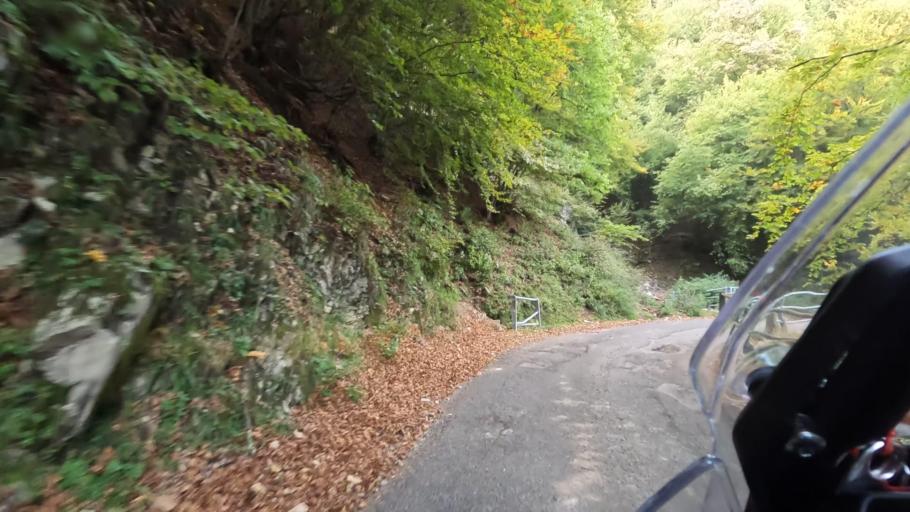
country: IT
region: Lombardy
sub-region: Provincia di Como
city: Pigra
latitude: 45.9762
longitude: 9.1245
